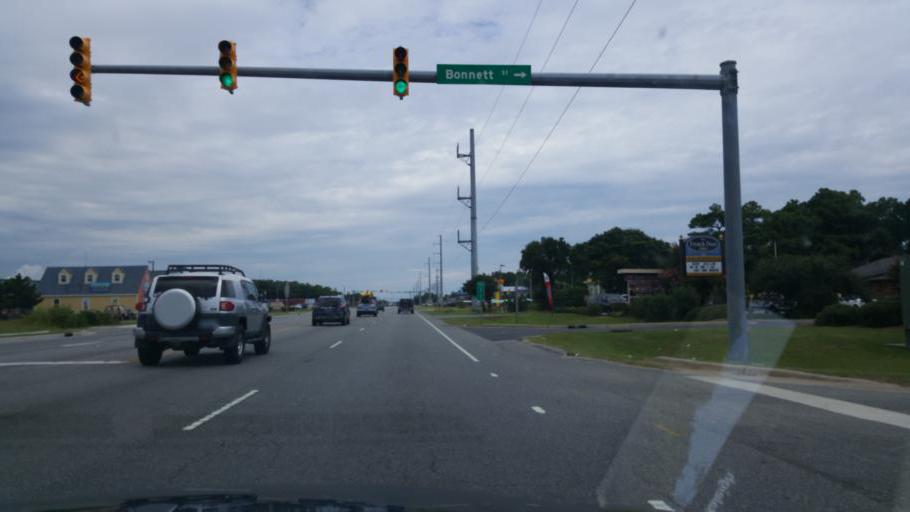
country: US
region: North Carolina
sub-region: Dare County
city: Nags Head
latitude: 35.9775
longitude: -75.6407
